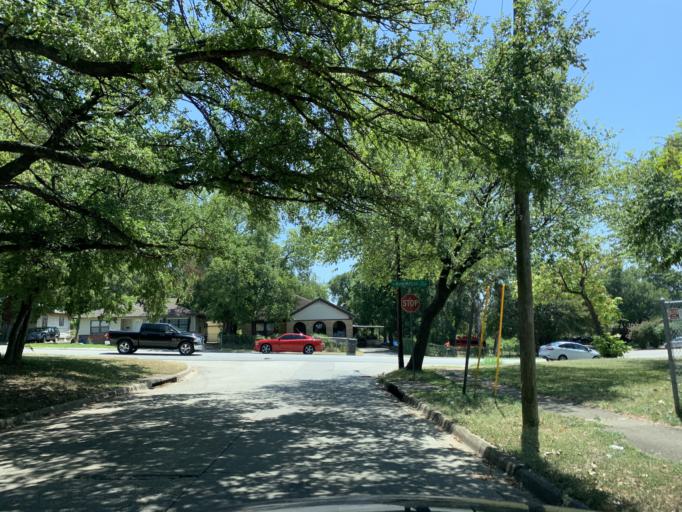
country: US
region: Texas
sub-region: Dallas County
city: Dallas
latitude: 32.6927
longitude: -96.8069
